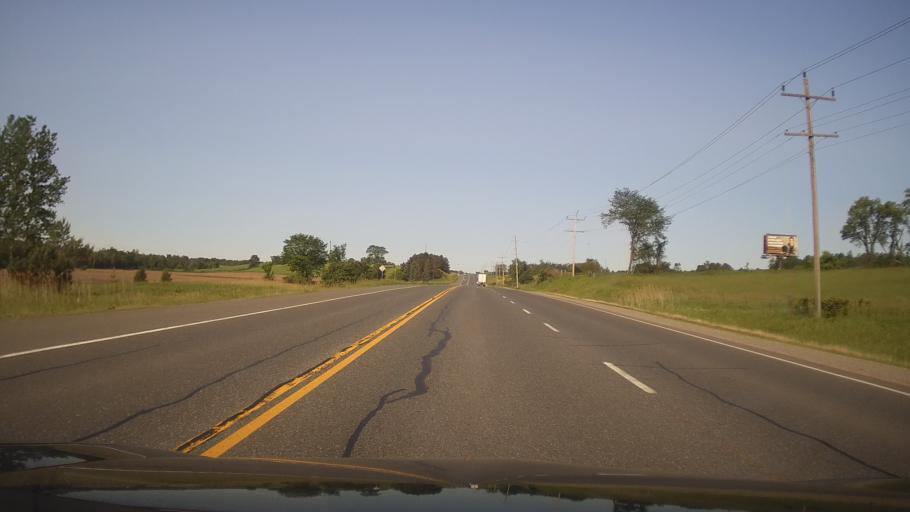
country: CA
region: Ontario
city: Peterborough
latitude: 44.3637
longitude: -78.0130
